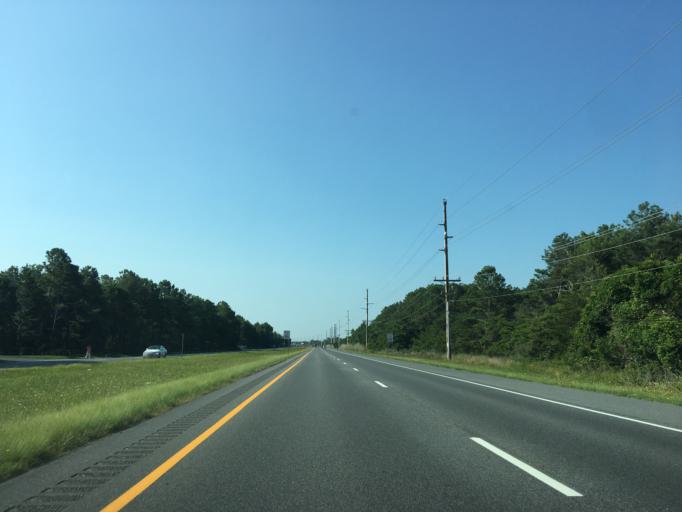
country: US
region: Delaware
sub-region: Sussex County
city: Bethany Beach
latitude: 38.5632
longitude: -75.0604
